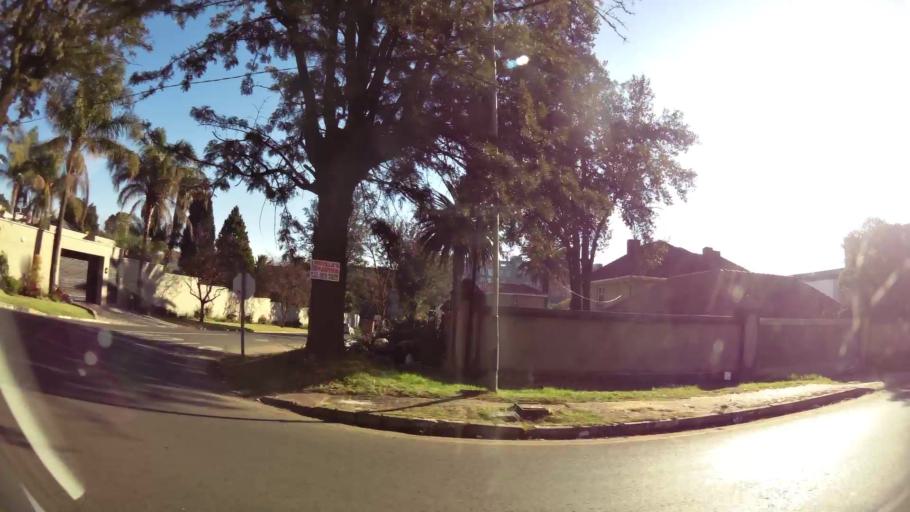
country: ZA
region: Gauteng
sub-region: City of Johannesburg Metropolitan Municipality
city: Johannesburg
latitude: -26.1690
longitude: 28.0717
